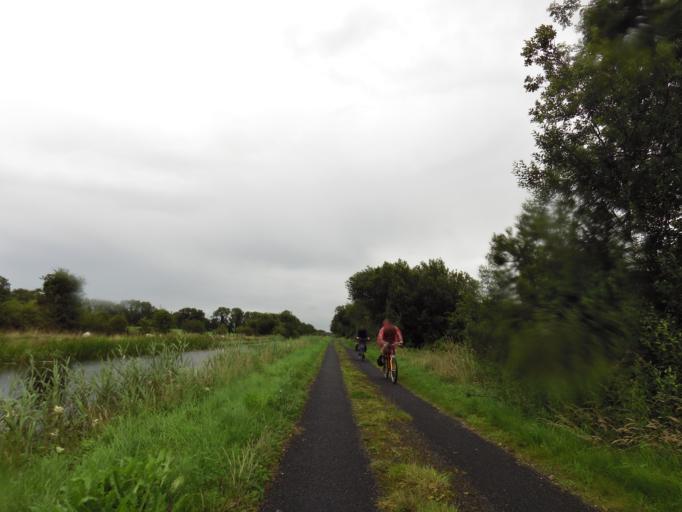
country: IE
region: Leinster
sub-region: An Longfort
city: Edgeworthstown
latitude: 53.5806
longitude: -7.5765
